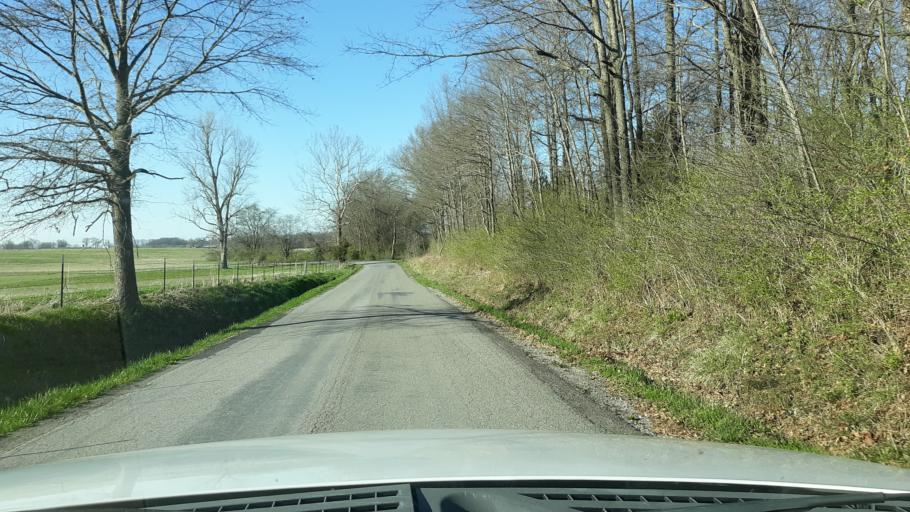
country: US
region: Illinois
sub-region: Saline County
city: Harrisburg
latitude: 37.7629
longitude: -88.5818
